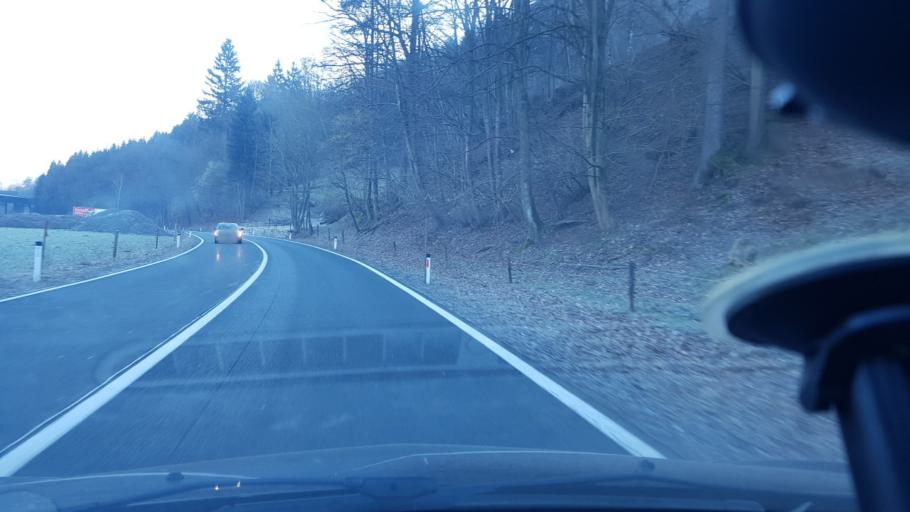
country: SI
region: Moravce
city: Moravce
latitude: 46.1732
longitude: 14.7974
